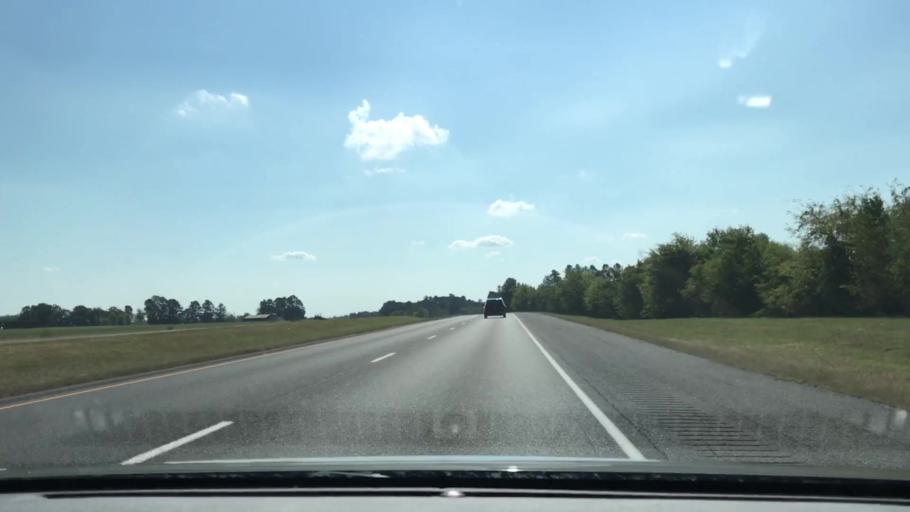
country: US
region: Kentucky
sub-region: Marshall County
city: Benton
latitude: 36.7975
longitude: -88.3385
